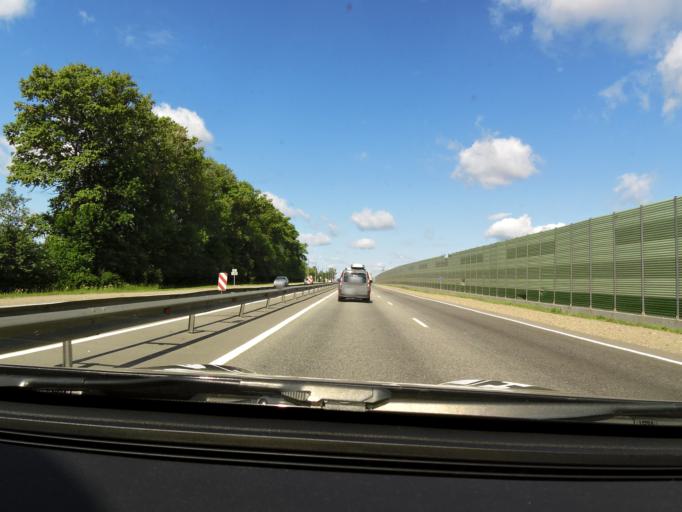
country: RU
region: Tverskaya
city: Likhoslavl'
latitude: 56.9093
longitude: 35.6220
